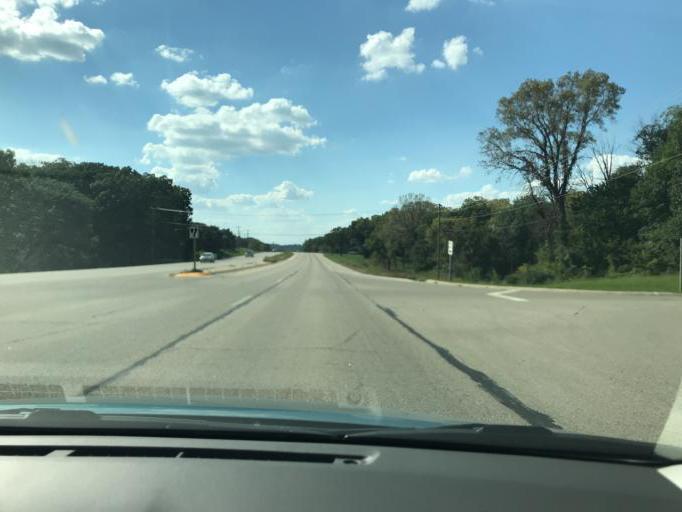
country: US
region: Wisconsin
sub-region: Walworth County
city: Como
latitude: 42.5830
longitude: -88.5041
